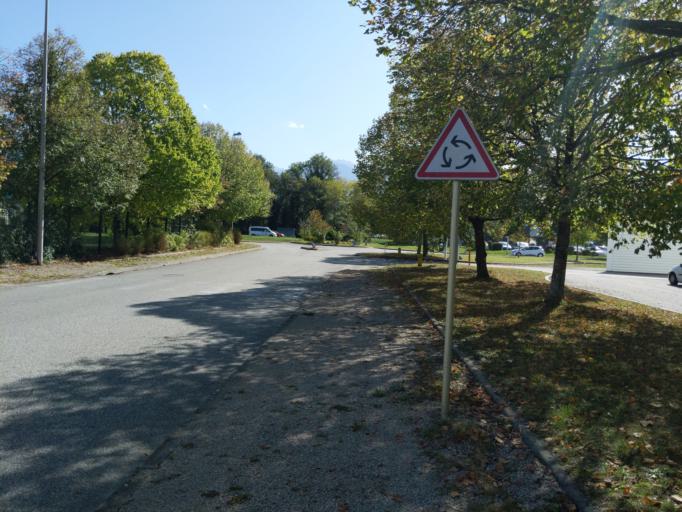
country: FR
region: Rhone-Alpes
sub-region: Departement de la Savoie
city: Montmelian
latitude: 45.4794
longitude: 6.0369
